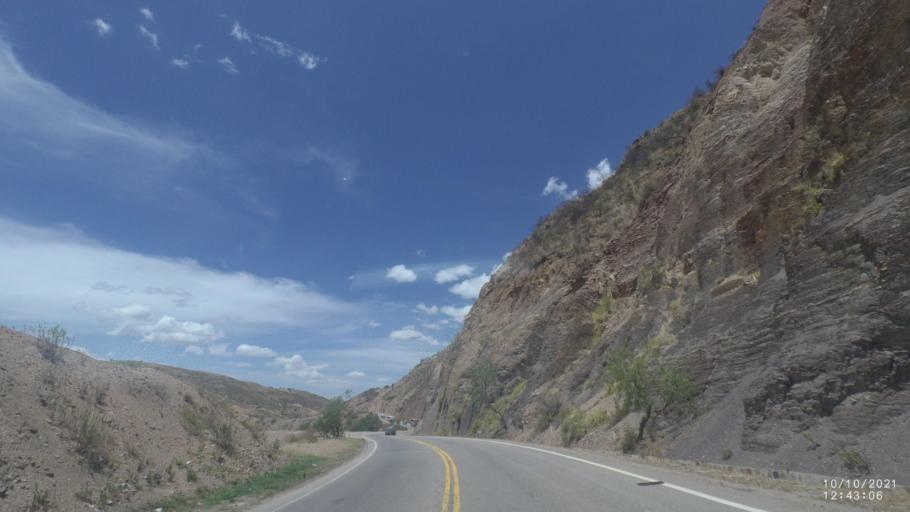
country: BO
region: Cochabamba
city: Irpa Irpa
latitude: -17.6286
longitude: -66.3890
